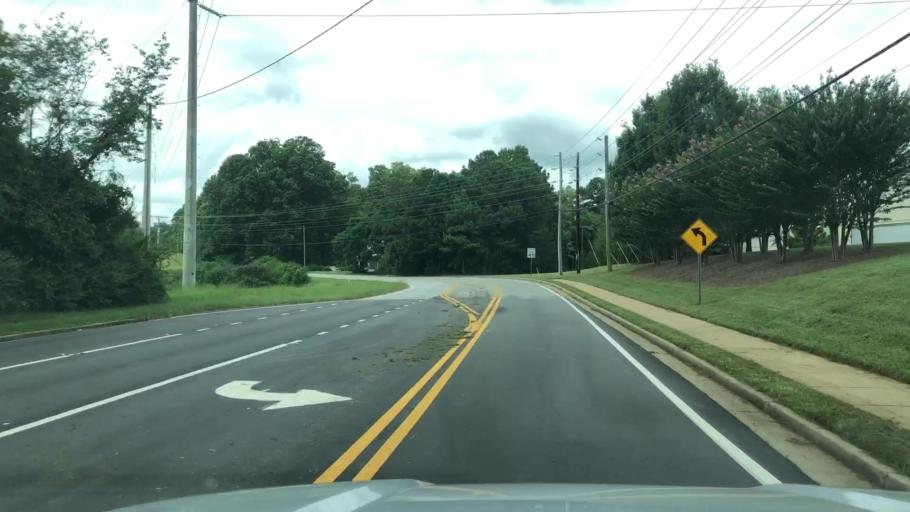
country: US
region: Georgia
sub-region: Gwinnett County
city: Suwanee
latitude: 34.0363
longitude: -84.0316
